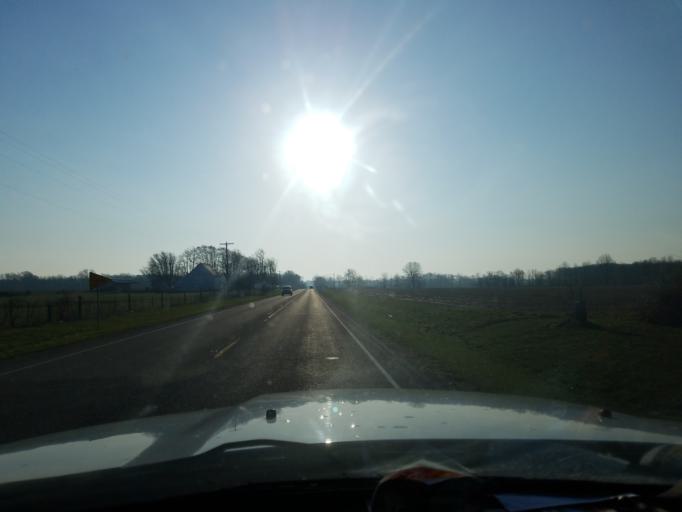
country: US
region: Indiana
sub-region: Vigo County
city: Seelyville
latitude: 39.3902
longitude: -87.2532
